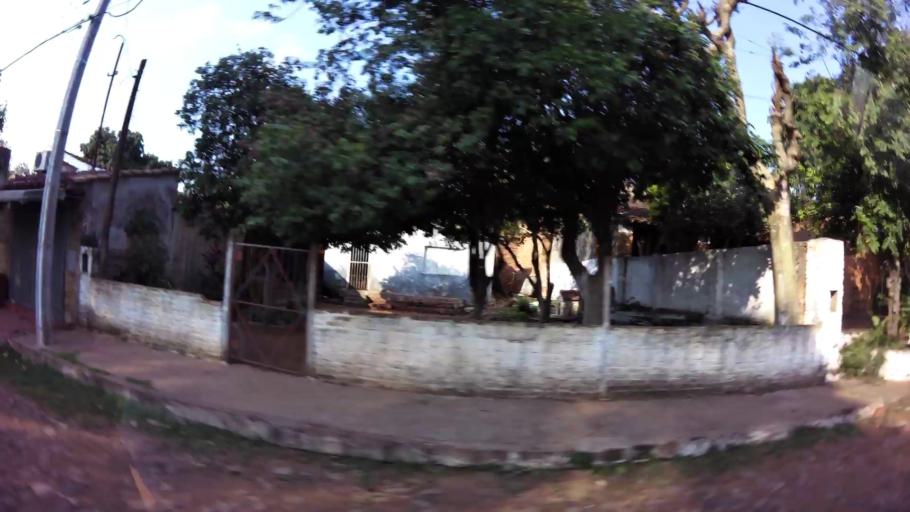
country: PY
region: Central
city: Lambare
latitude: -25.3493
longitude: -57.5883
